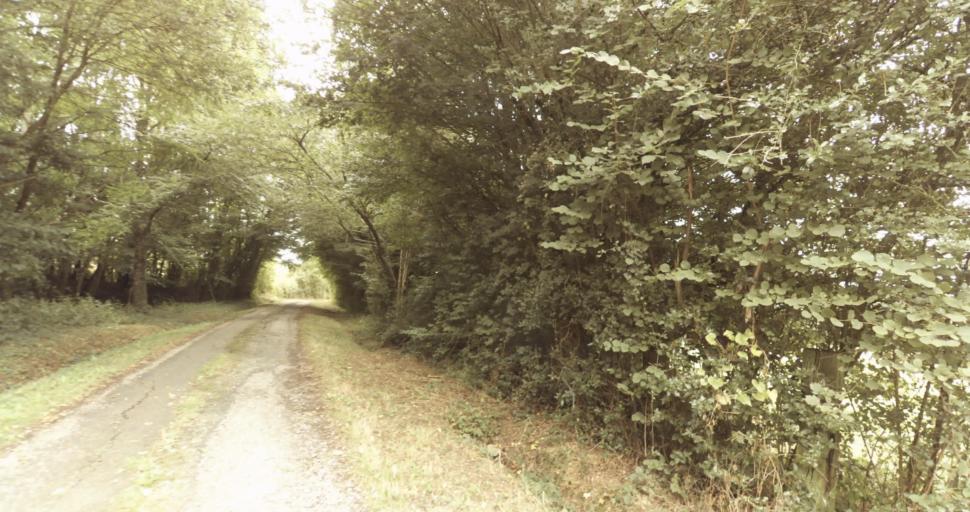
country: FR
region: Lower Normandy
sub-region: Departement de l'Orne
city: Sainte-Gauburge-Sainte-Colombe
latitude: 48.7126
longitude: 0.4535
